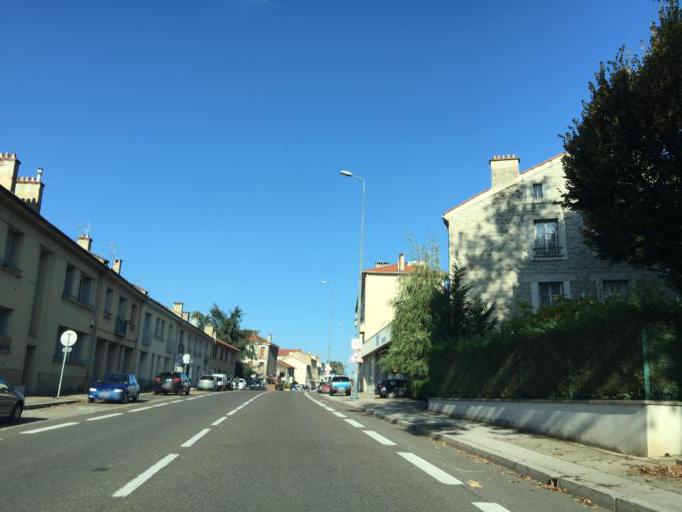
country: FR
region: Rhone-Alpes
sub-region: Departement de la Loire
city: Saint-Etienne
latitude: 45.4478
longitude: 4.4044
